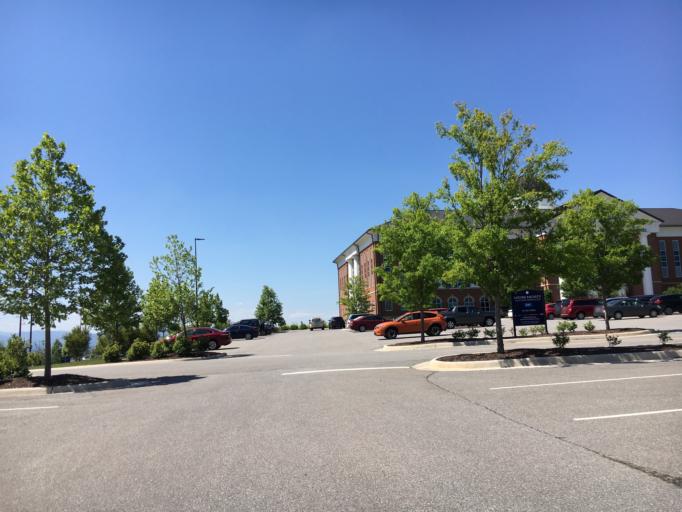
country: US
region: Virginia
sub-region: City of Lynchburg
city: West Lynchburg
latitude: 37.3361
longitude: -79.1796
